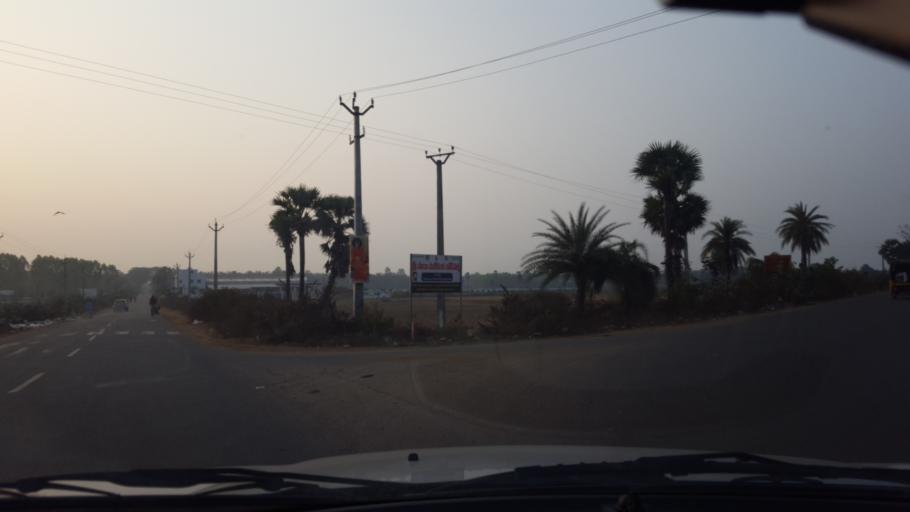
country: IN
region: Andhra Pradesh
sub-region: Srikakulam
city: Amudalavalasa
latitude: 18.3848
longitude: 83.9240
